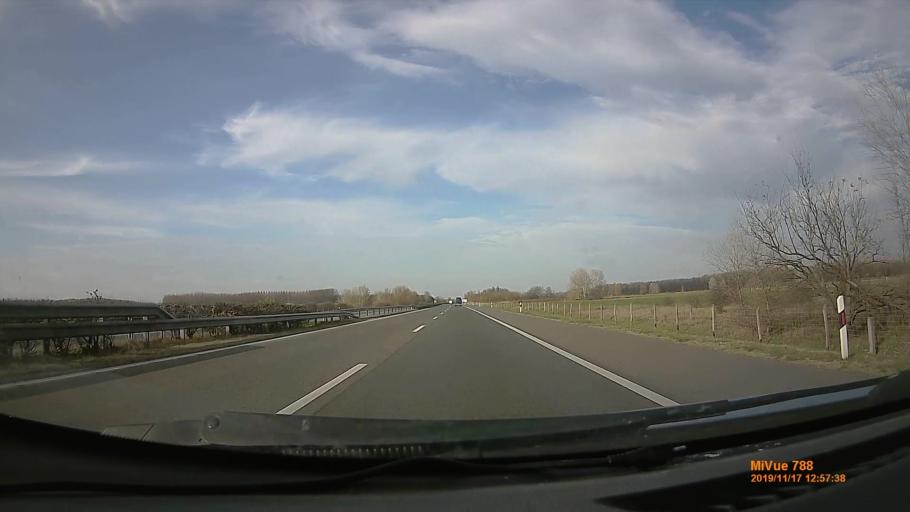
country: HU
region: Pest
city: Hernad
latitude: 47.1888
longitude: 19.4305
